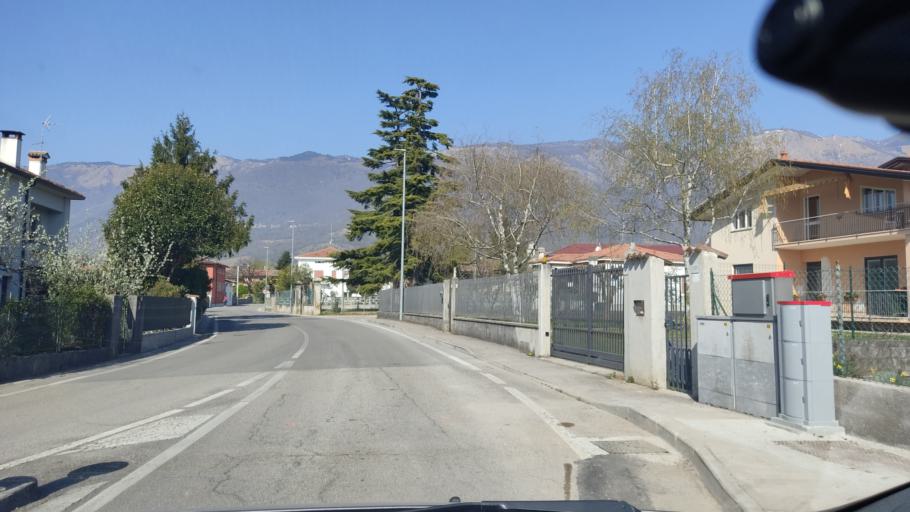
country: IT
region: Friuli Venezia Giulia
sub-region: Provincia di Pordenone
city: Budoia
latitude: 46.0414
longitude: 12.5361
